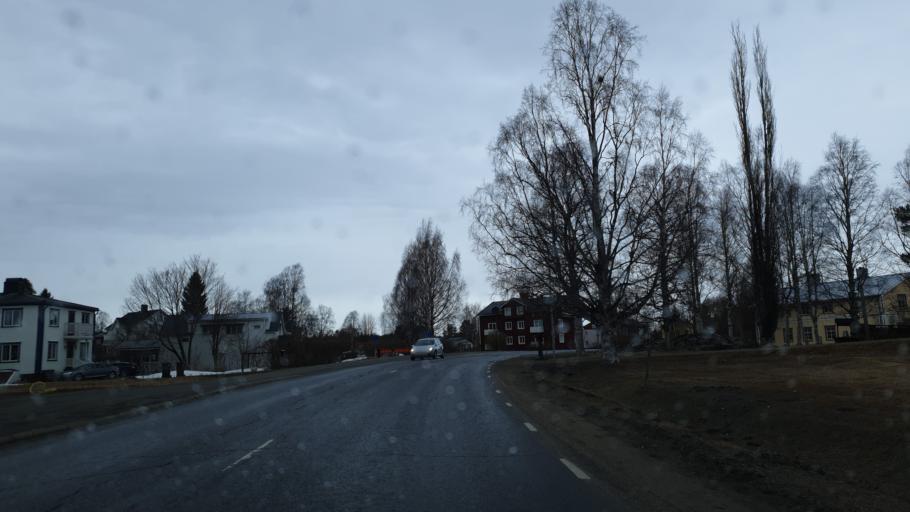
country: SE
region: Vaesterbotten
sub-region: Skelleftea Kommun
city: Kage
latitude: 64.8358
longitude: 20.9846
